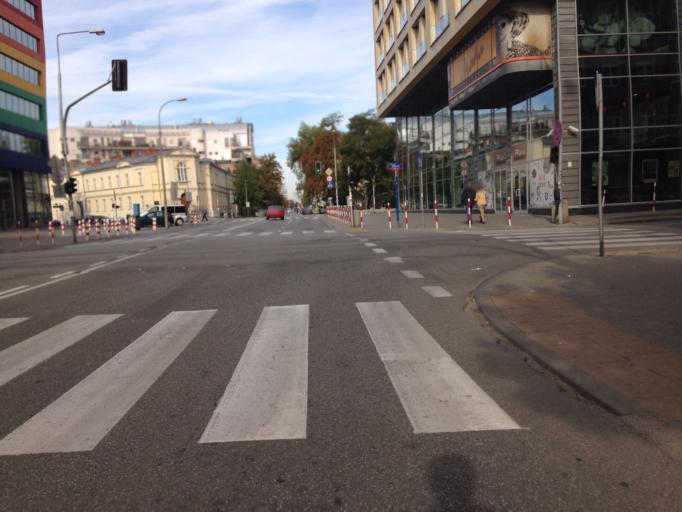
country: PL
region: Masovian Voivodeship
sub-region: Warszawa
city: Praga Polnoc
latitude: 52.2512
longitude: 21.0358
